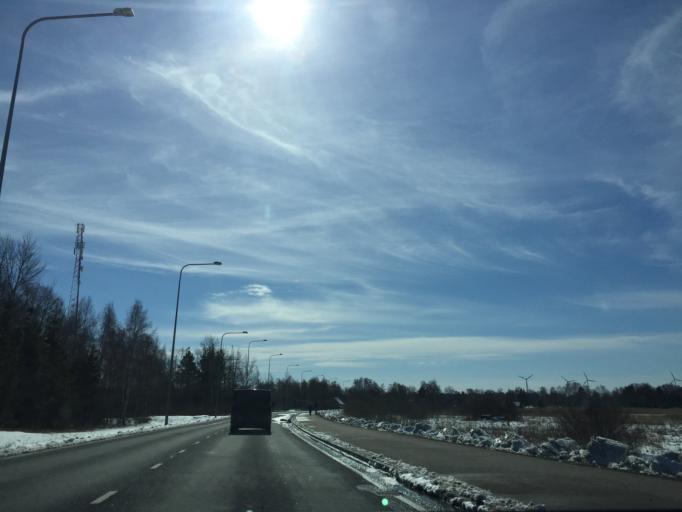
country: EE
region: Laeaene
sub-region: Lihula vald
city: Lihula
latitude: 58.5765
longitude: 23.5239
